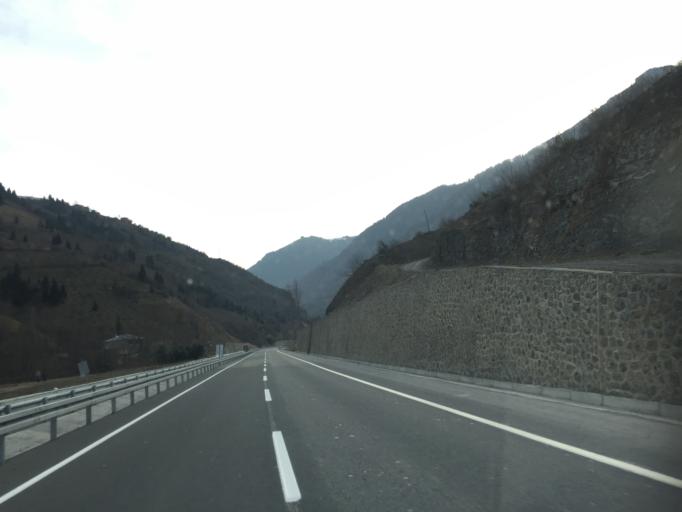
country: TR
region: Trabzon
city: Macka
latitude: 40.7888
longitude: 39.5792
